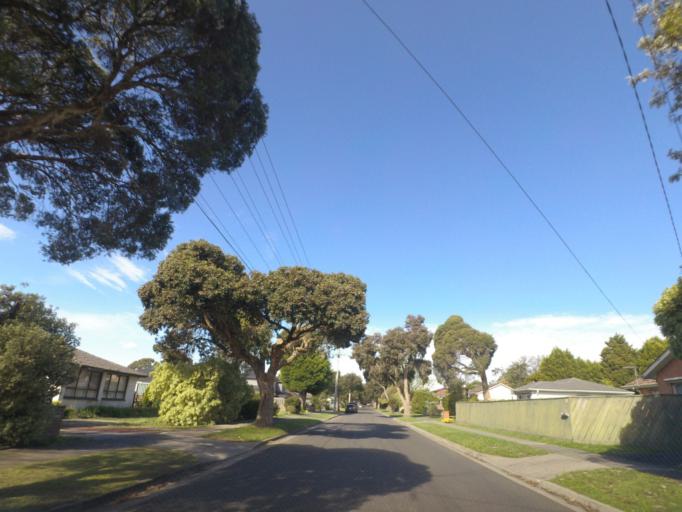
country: AU
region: Victoria
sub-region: Knox
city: Knoxfield
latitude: -37.8841
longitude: 145.2540
